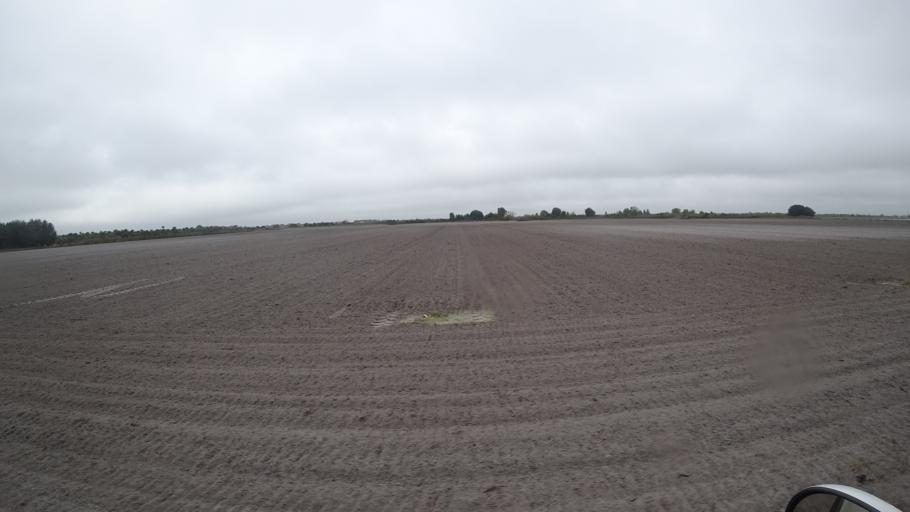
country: US
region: Florida
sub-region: Sarasota County
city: Warm Mineral Springs
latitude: 27.2827
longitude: -82.1754
